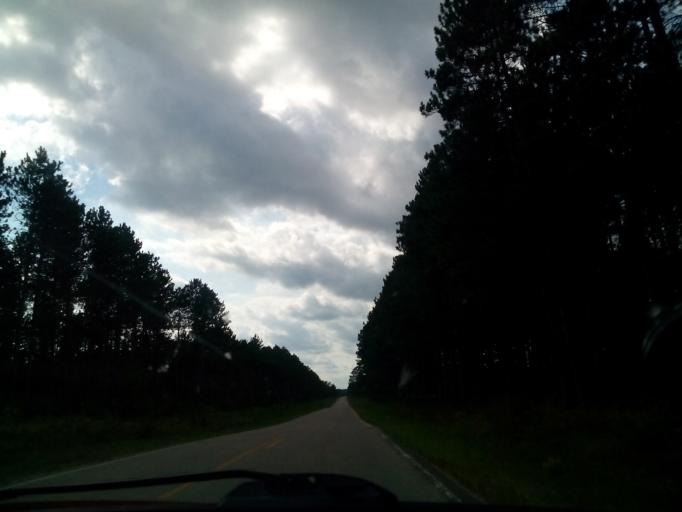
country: US
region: Michigan
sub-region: Dickinson County
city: Kingsford
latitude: 45.4021
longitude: -88.2248
